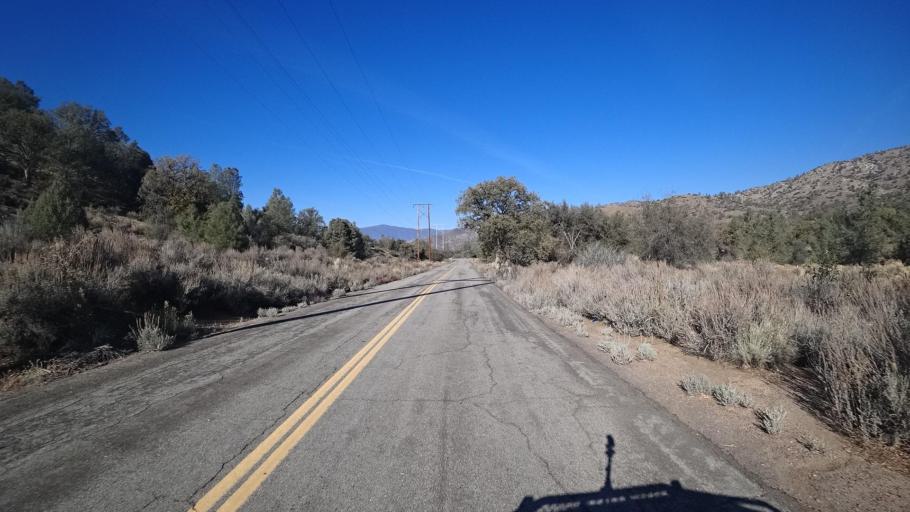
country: US
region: California
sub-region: Kern County
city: Bodfish
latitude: 35.3878
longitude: -118.4252
